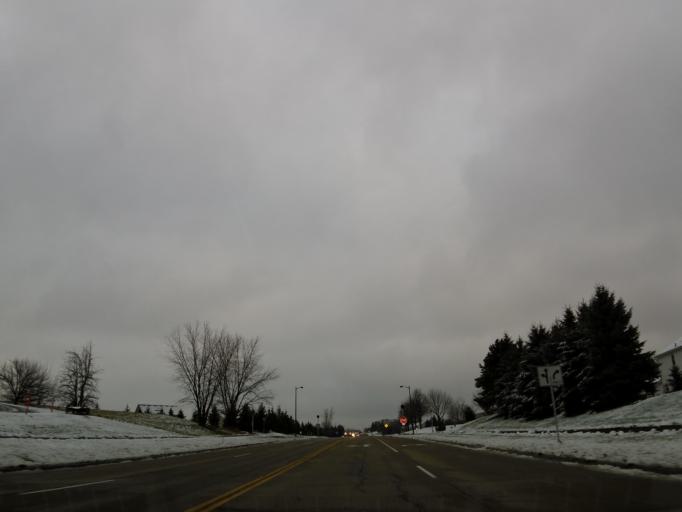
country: US
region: Minnesota
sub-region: Dakota County
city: Apple Valley
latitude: 44.6968
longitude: -93.2379
